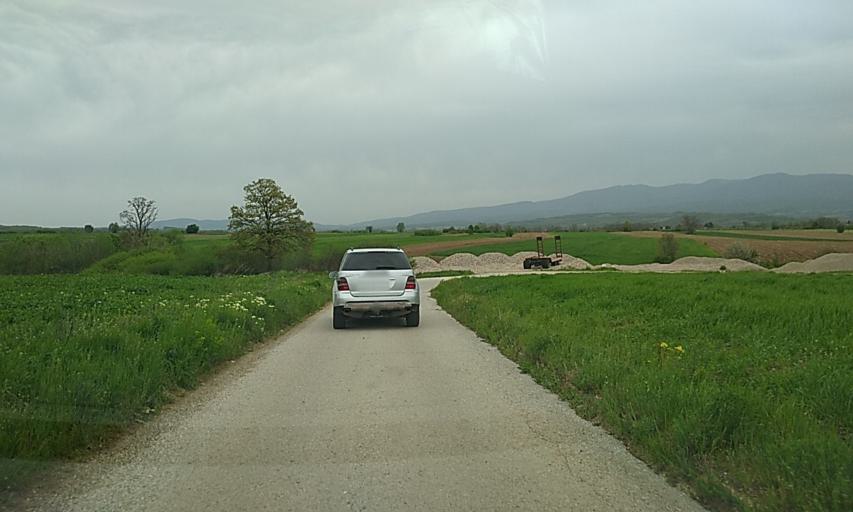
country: RS
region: Central Serbia
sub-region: Nisavski Okrug
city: Razanj
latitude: 43.5701
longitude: 21.5150
